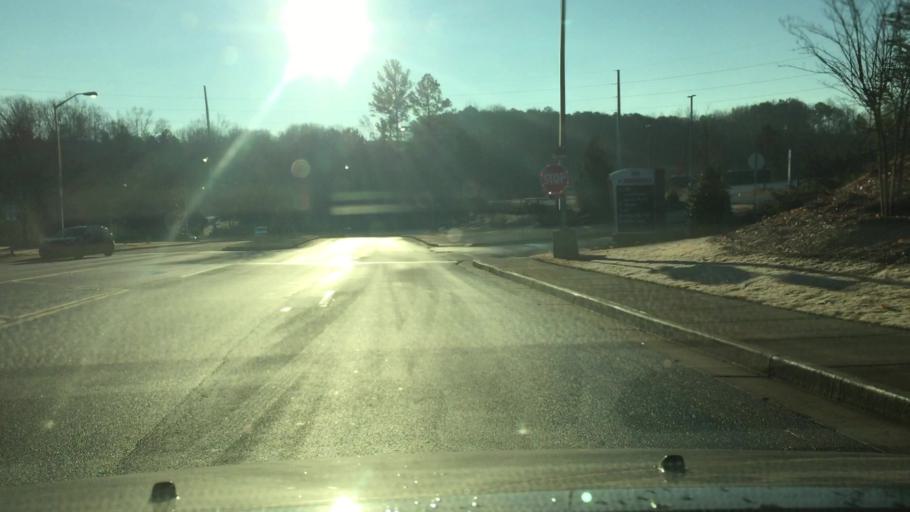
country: US
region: Georgia
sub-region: Forsyth County
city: Cumming
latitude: 34.1754
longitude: -84.1405
